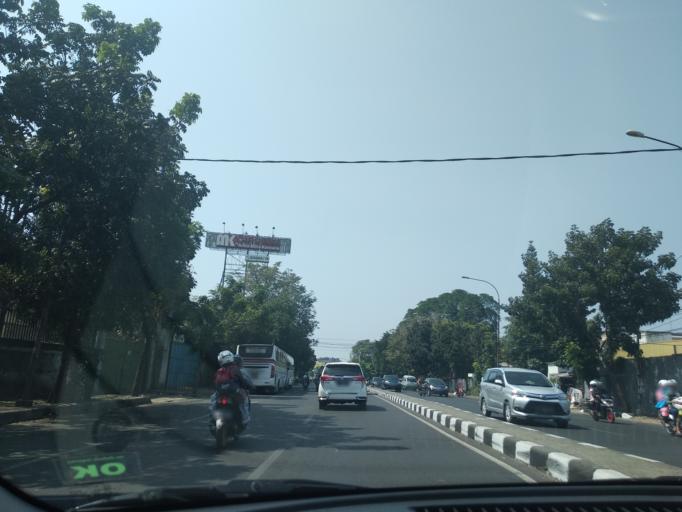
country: ID
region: West Java
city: Margahayukencana
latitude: -6.9462
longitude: 107.5913
